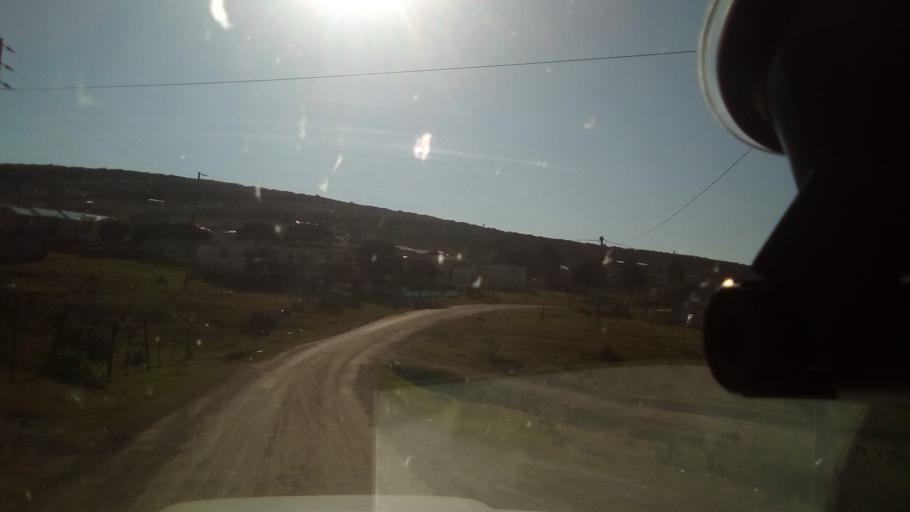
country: ZA
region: Eastern Cape
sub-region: Buffalo City Metropolitan Municipality
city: Bhisho
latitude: -32.8152
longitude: 27.3531
